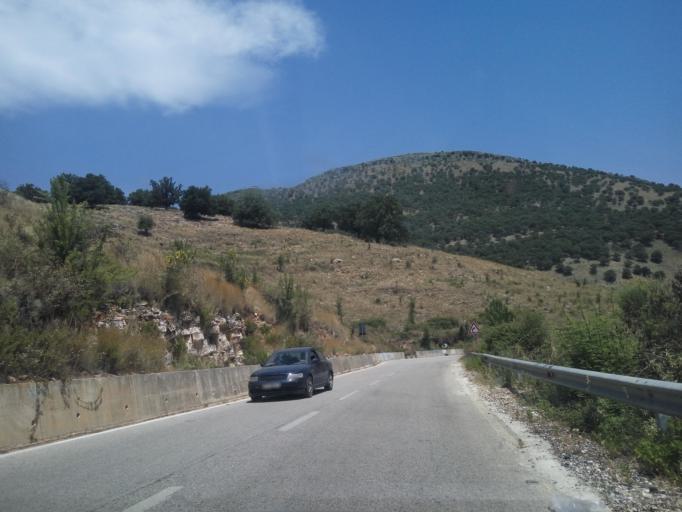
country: AL
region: Vlore
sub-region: Rrethi i Vlores
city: Himare
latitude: 40.0754
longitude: 19.7723
